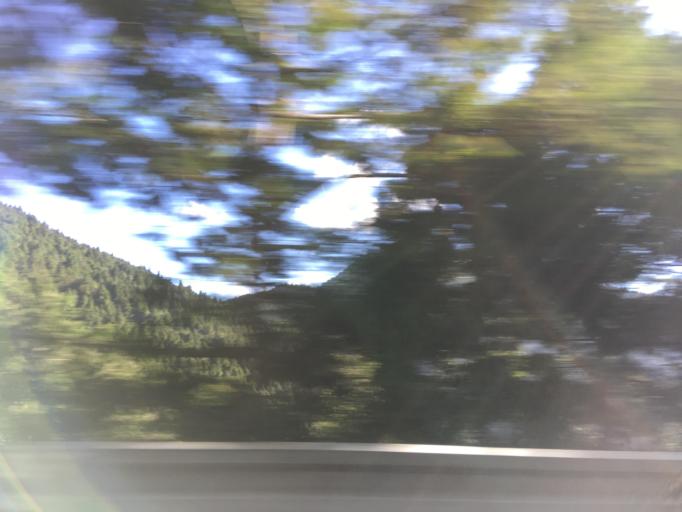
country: TW
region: Taiwan
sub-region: Yilan
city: Yilan
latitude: 24.4951
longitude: 121.5517
